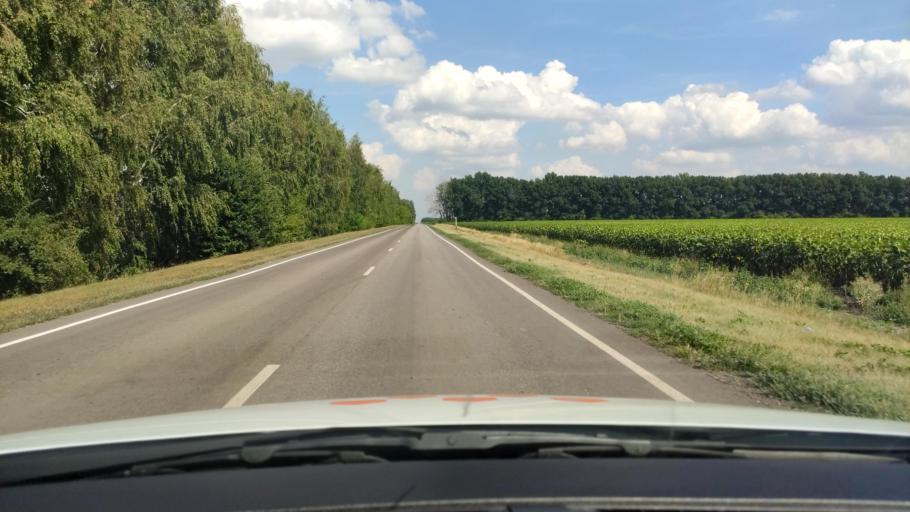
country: RU
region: Voronezj
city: Ertil'
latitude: 51.7946
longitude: 40.7050
